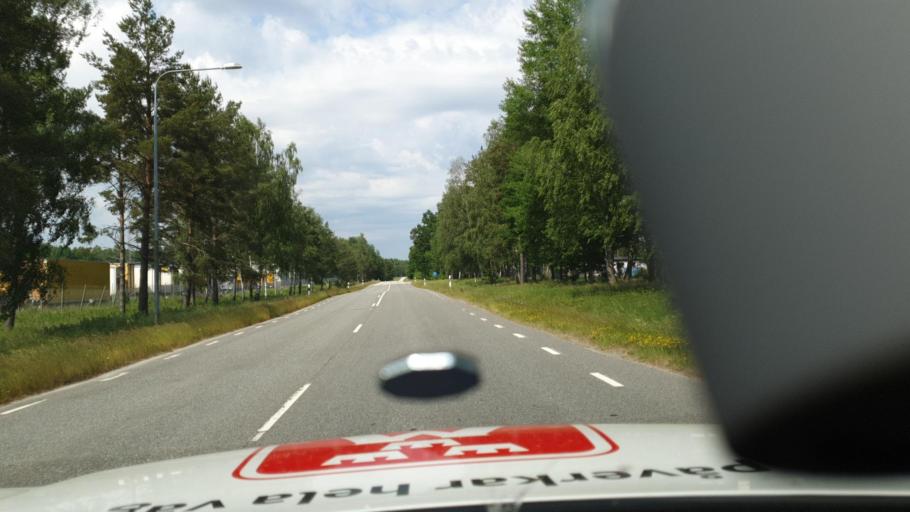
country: SE
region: Joenkoeping
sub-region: Varnamo Kommun
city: Varnamo
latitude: 57.2136
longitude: 14.0403
